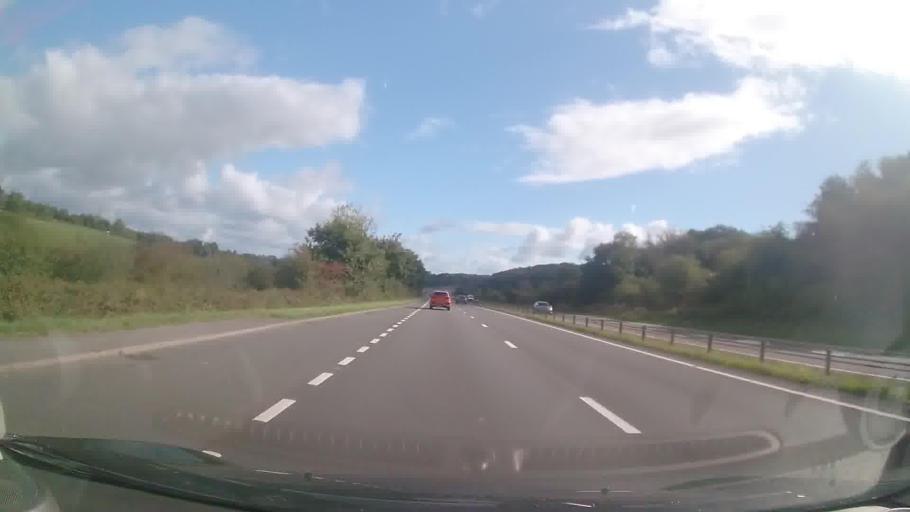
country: GB
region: Wales
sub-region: Carmarthenshire
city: Carmarthen
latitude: 51.8411
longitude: -4.2701
